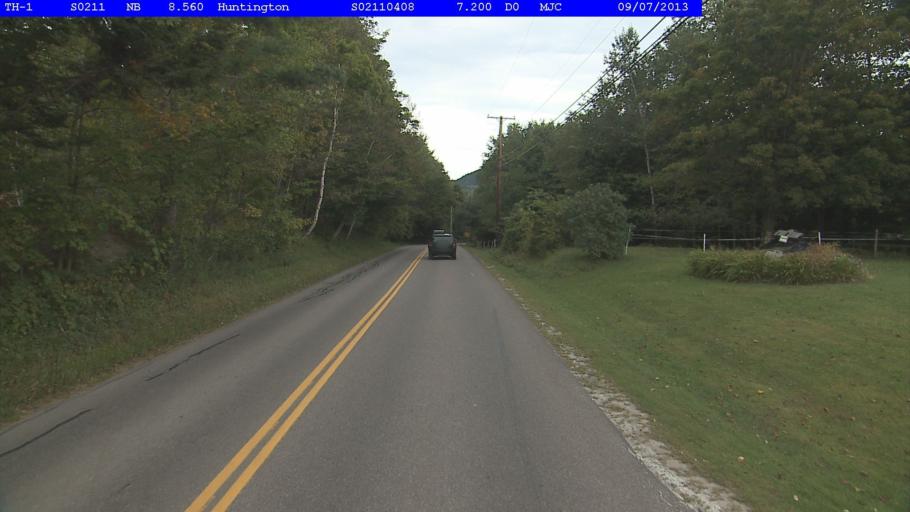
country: US
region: Vermont
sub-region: Chittenden County
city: Hinesburg
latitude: 44.3224
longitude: -72.9887
